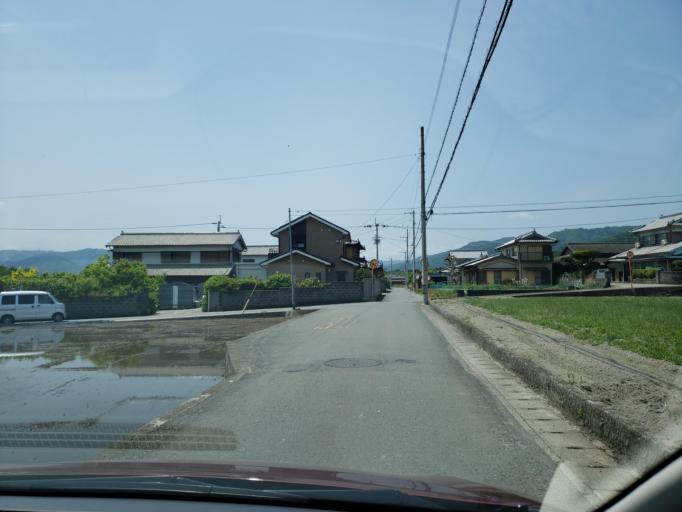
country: JP
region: Tokushima
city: Wakimachi
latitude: 34.0864
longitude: 134.2126
